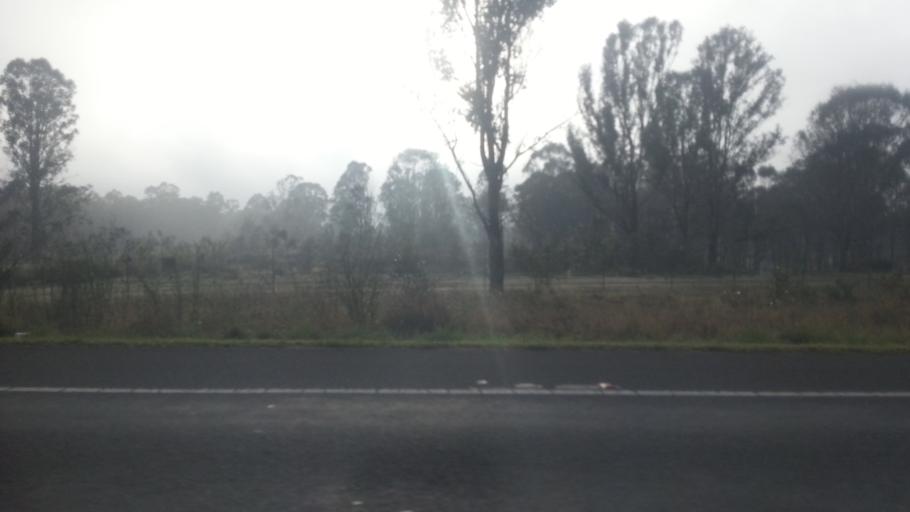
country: AU
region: New South Wales
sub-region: Penrith Municipality
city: Mulgoa
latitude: -33.8278
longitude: 150.6832
